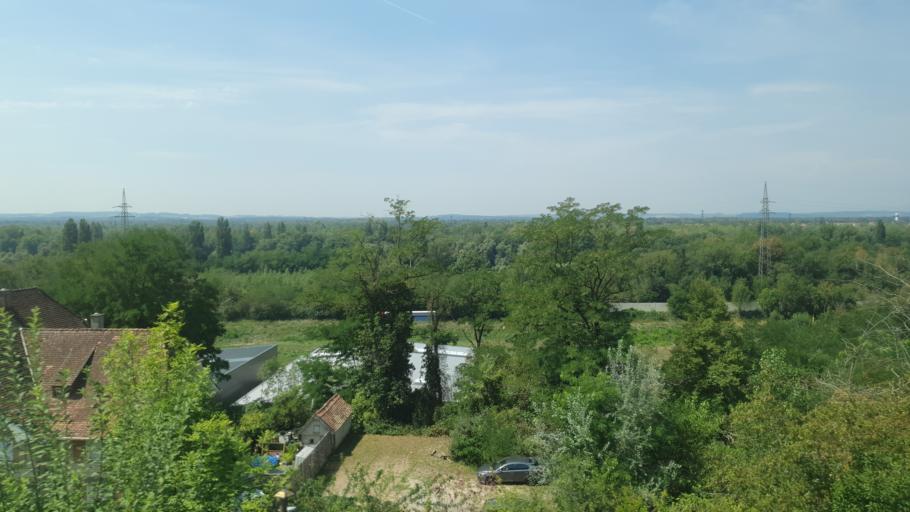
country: FR
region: Alsace
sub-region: Departement du Haut-Rhin
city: Kembs
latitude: 47.6823
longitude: 7.5257
